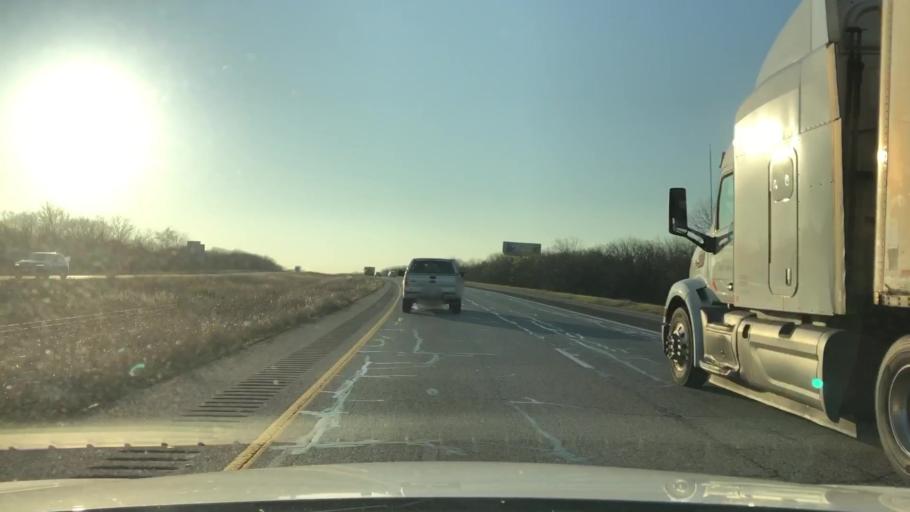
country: US
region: Texas
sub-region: Caldwell County
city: Luling
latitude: 29.6517
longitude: -97.6728
